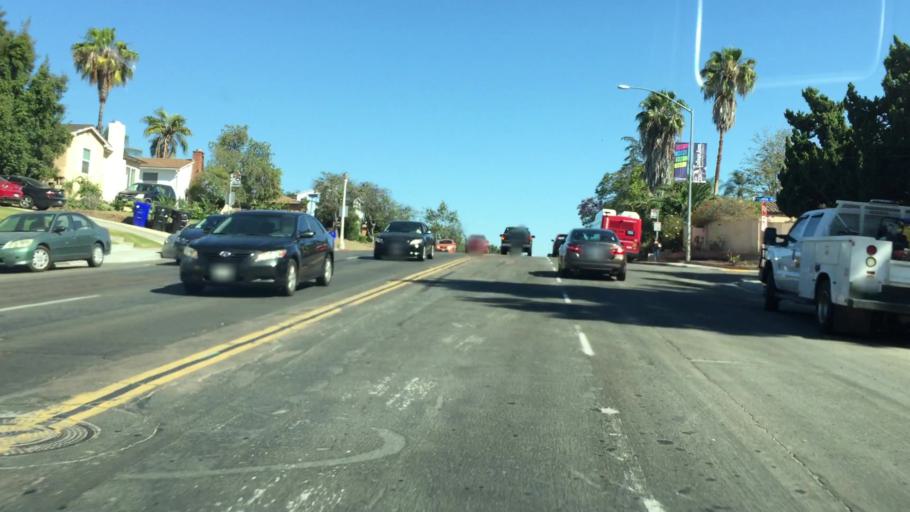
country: US
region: California
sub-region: San Diego County
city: La Mesa
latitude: 32.7690
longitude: -117.0689
